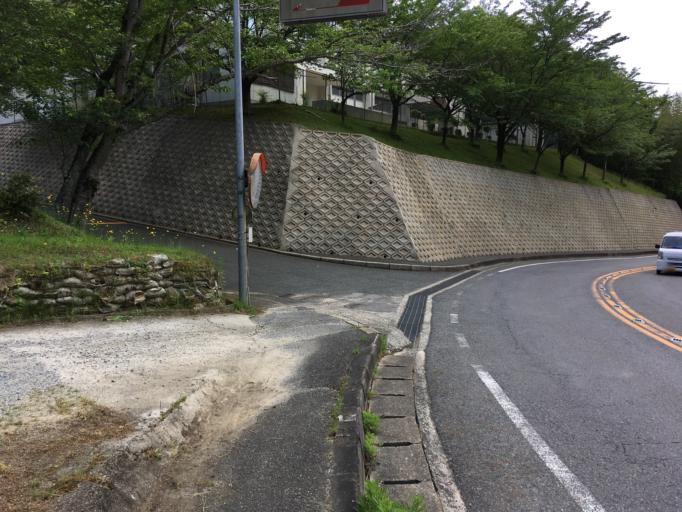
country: JP
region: Nara
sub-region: Ikoma-shi
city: Ikoma
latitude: 34.7089
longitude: 135.7120
